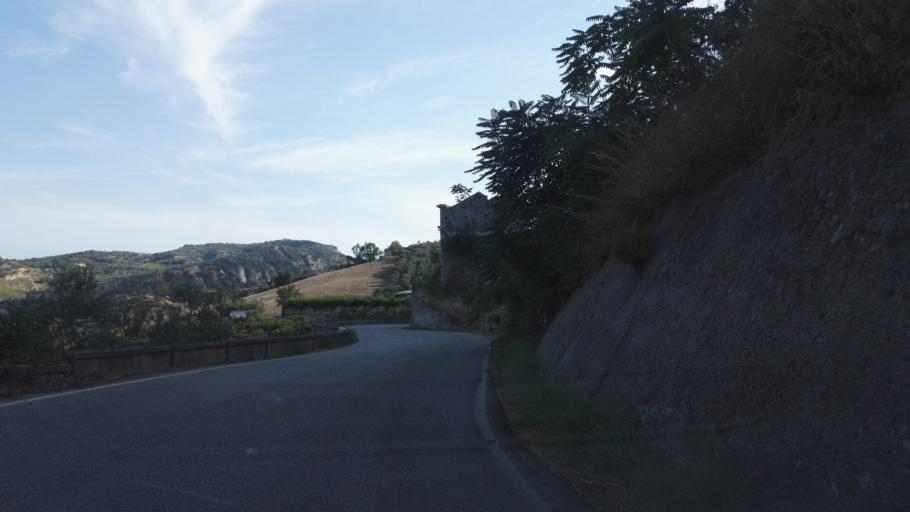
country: IT
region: Calabria
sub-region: Provincia di Reggio Calabria
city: Stilo
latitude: 38.4786
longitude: 16.4792
